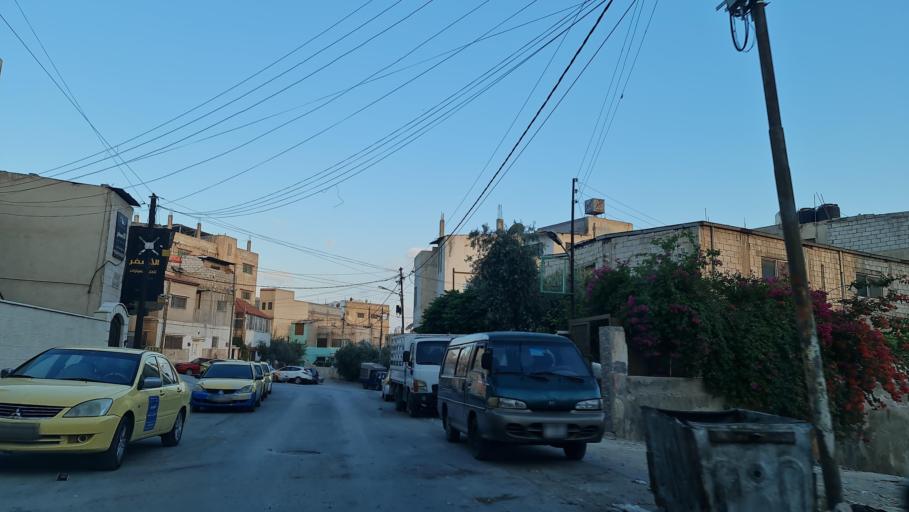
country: JO
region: Zarqa
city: Zarqa
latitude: 32.0762
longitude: 36.0818
